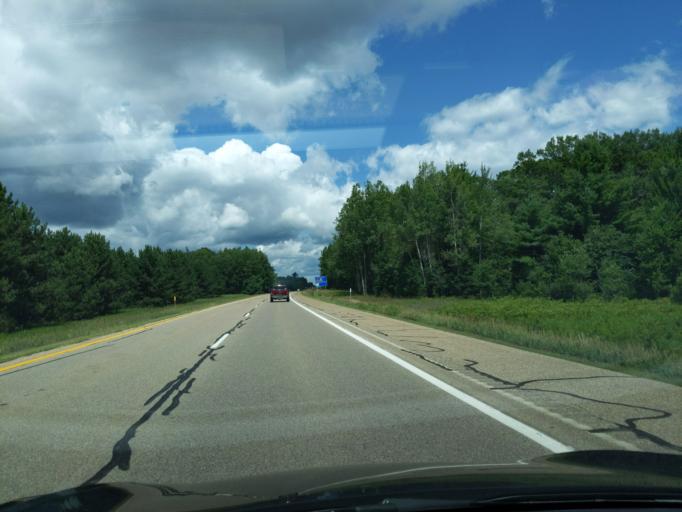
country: US
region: Michigan
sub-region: Roscommon County
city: Houghton Lake
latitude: 44.3111
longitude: -84.8051
